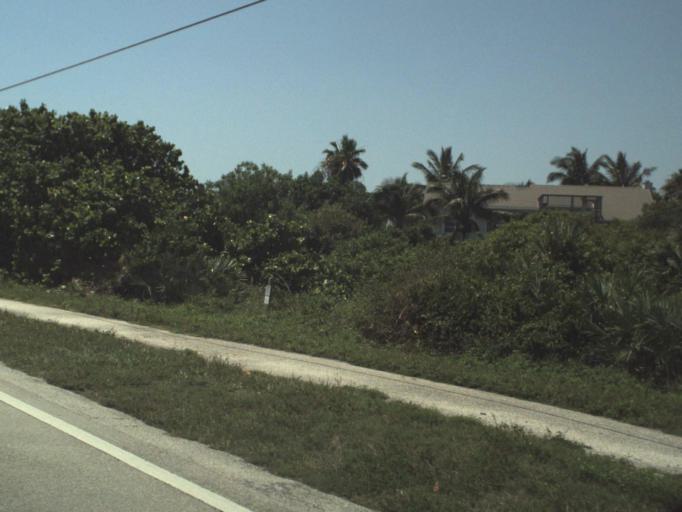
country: US
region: Florida
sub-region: Brevard County
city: Malabar
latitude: 27.9919
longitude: -80.5208
